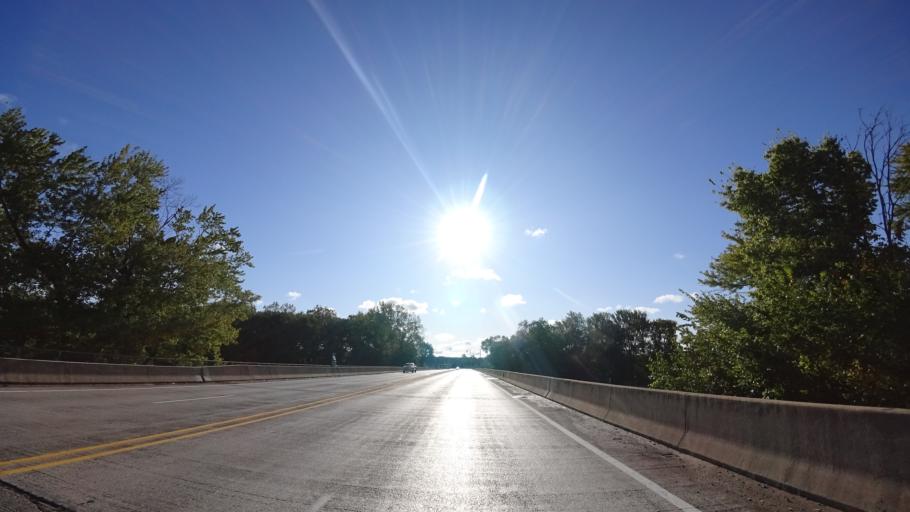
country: US
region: Michigan
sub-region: Kent County
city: Grandville
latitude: 42.9154
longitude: -85.7678
